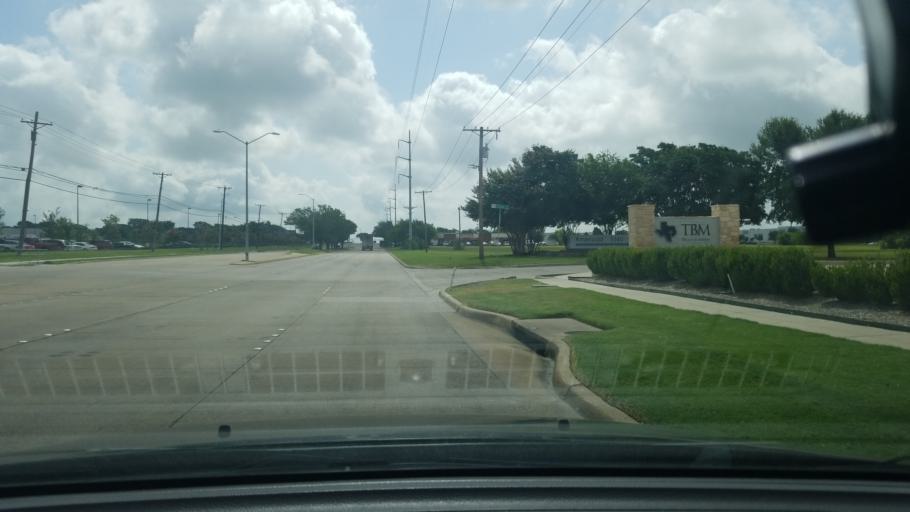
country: US
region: Texas
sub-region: Dallas County
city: Mesquite
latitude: 32.7922
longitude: -96.6756
